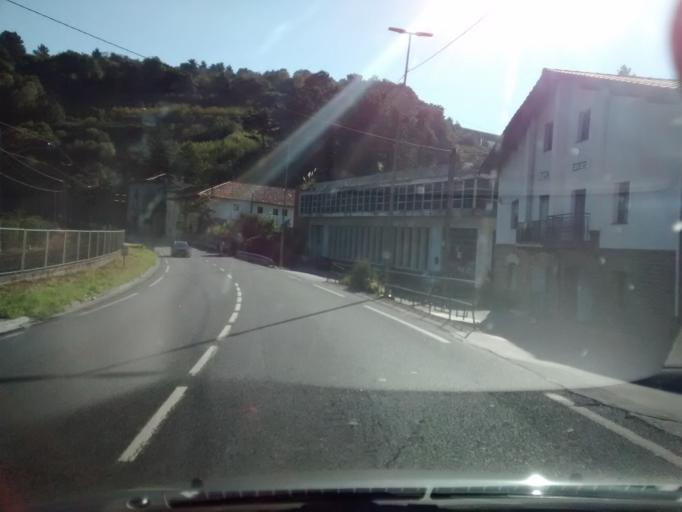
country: ES
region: Basque Country
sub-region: Provincia de Guipuzcoa
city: Deba
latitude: 43.2890
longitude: -2.3620
